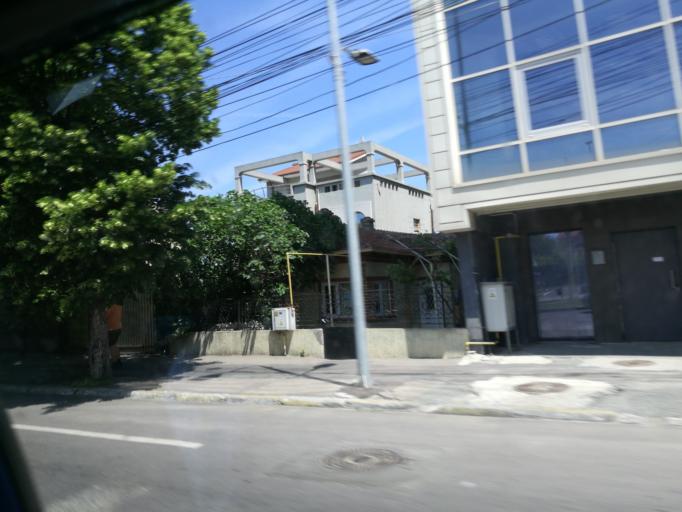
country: RO
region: Constanta
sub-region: Municipiul Constanta
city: Constanta
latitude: 44.1986
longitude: 28.6477
